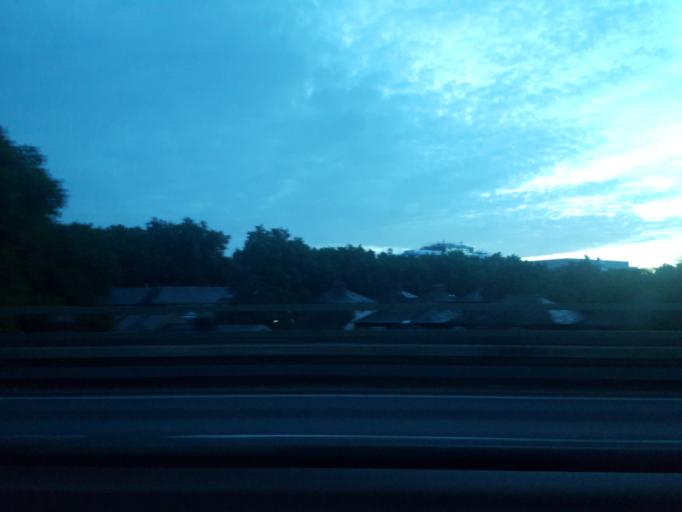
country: GB
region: England
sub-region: Greater London
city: Acton
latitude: 51.4907
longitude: -0.2806
